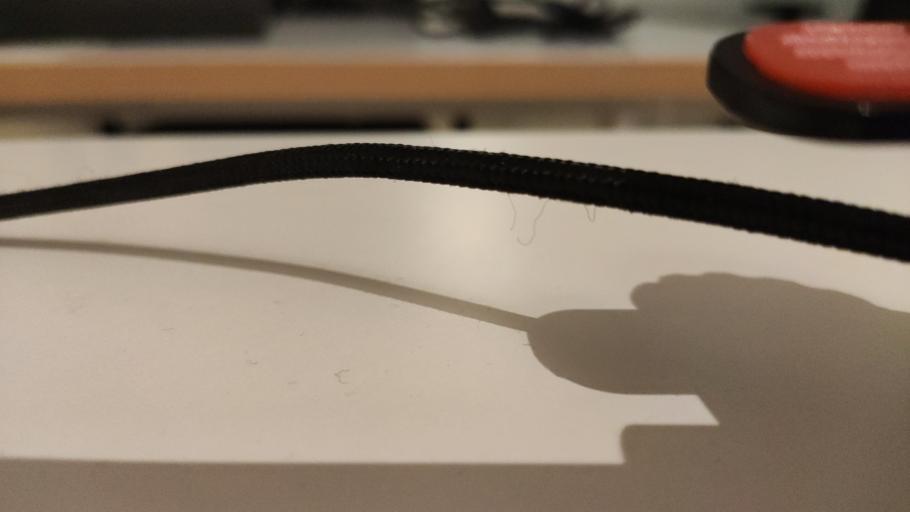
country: RU
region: Moskovskaya
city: Novoye
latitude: 55.6584
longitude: 38.9384
